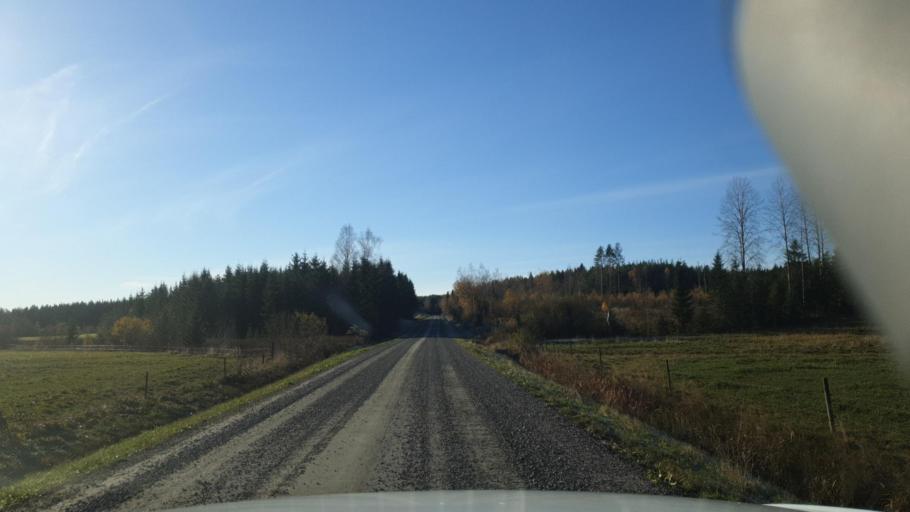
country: SE
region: Vaermland
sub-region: Karlstads Kommun
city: Edsvalla
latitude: 59.5522
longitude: 13.0112
